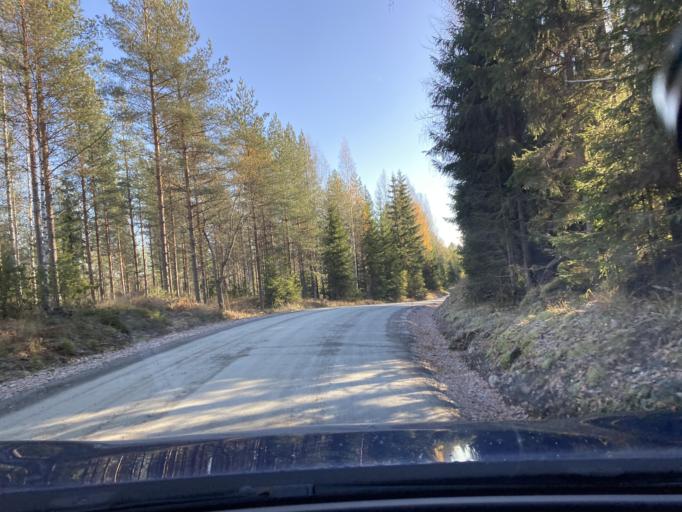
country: FI
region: Haeme
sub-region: Haemeenlinna
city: Kalvola
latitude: 60.9900
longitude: 24.0367
